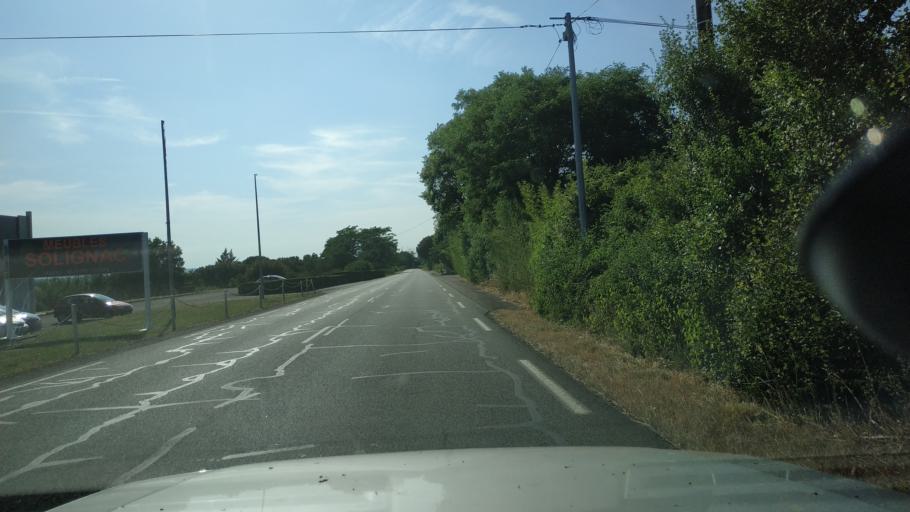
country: FR
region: Midi-Pyrenees
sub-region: Departement du Lot
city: Gramat
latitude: 44.7949
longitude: 1.6917
